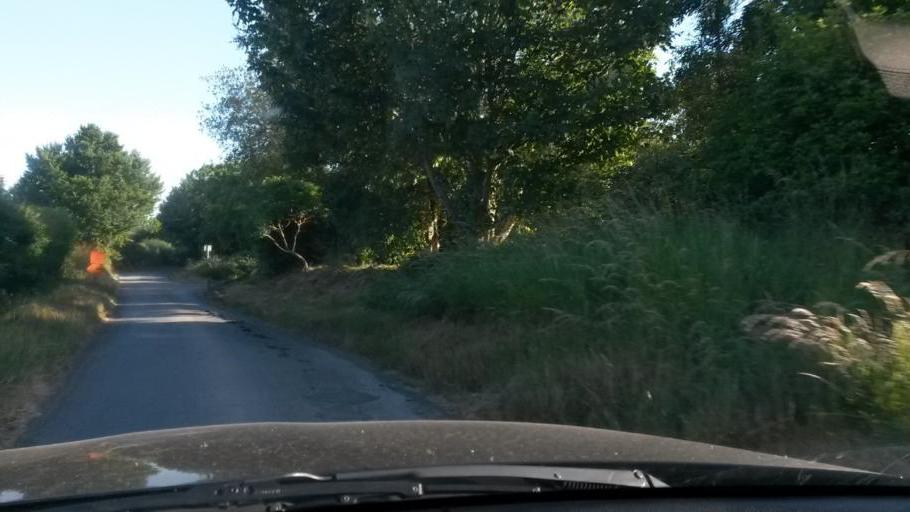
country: IE
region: Leinster
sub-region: An Mhi
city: Ashbourne
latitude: 53.5051
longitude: -6.3027
